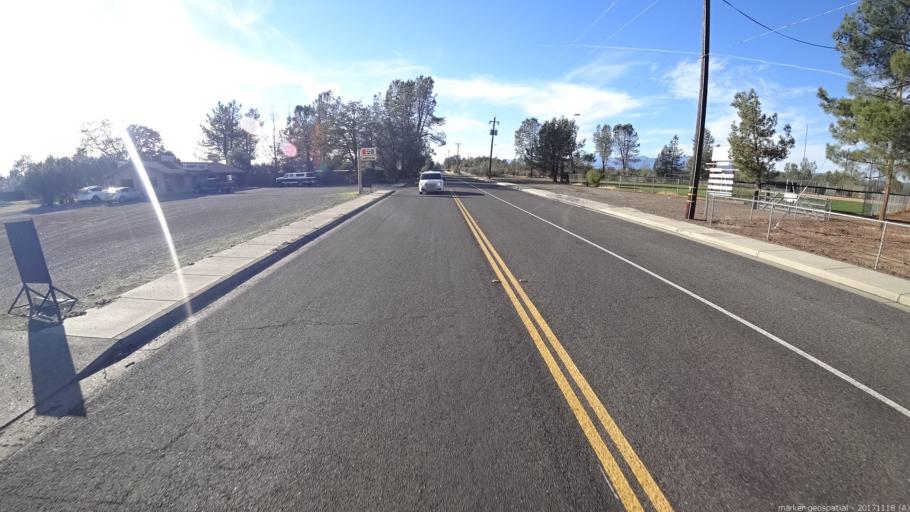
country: US
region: California
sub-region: Shasta County
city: Anderson
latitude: 40.4466
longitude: -122.4114
